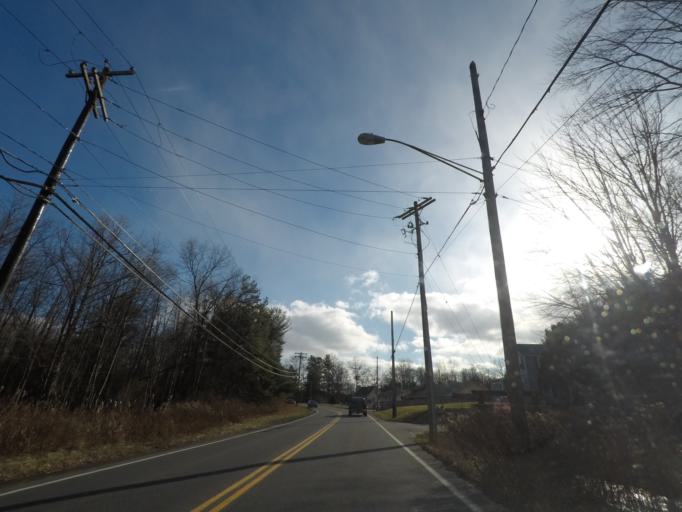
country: US
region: New York
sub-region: Albany County
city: Colonie
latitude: 42.7323
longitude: -73.8636
